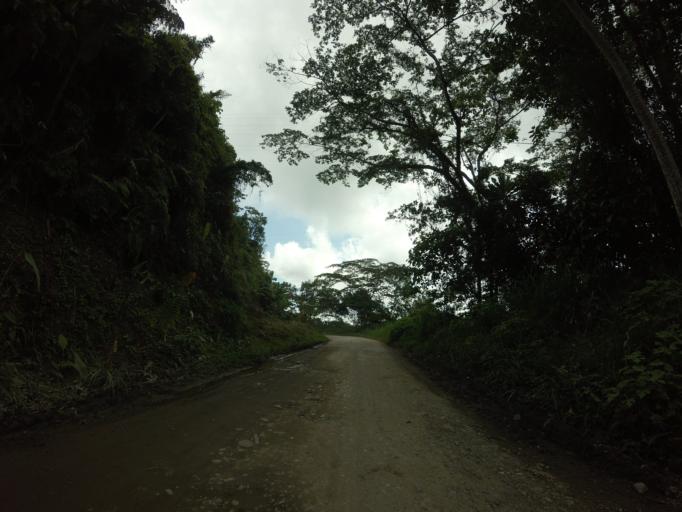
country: CO
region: Caldas
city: Victoria
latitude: 5.3112
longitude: -74.9674
